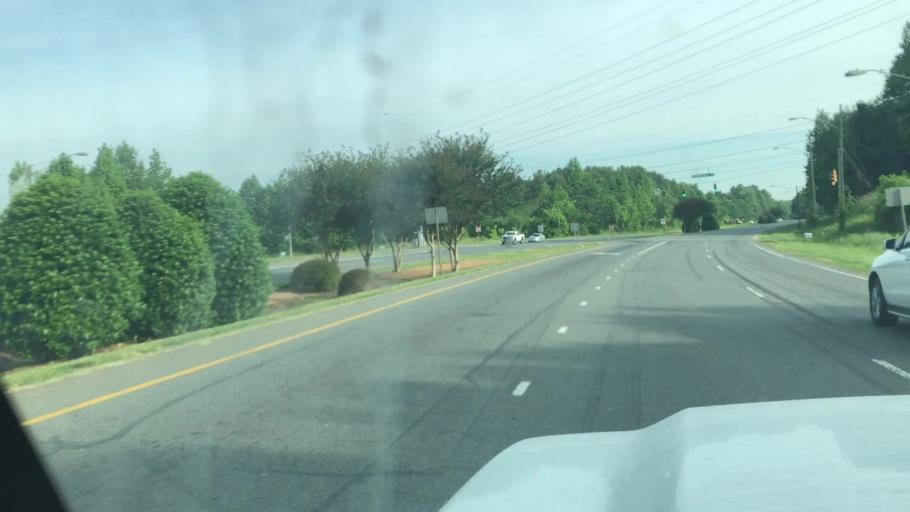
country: US
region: North Carolina
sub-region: Gaston County
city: Mount Holly
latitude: 35.2966
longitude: -80.9193
